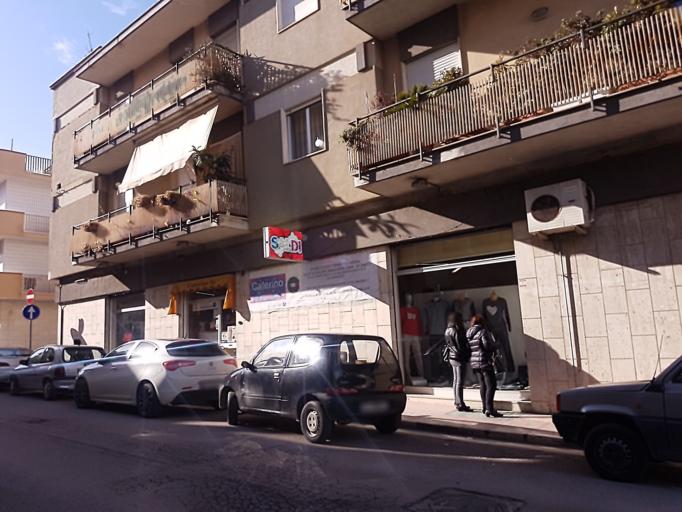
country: IT
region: Apulia
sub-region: Provincia di Barletta - Andria - Trani
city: Andria
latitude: 41.2319
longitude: 16.2913
